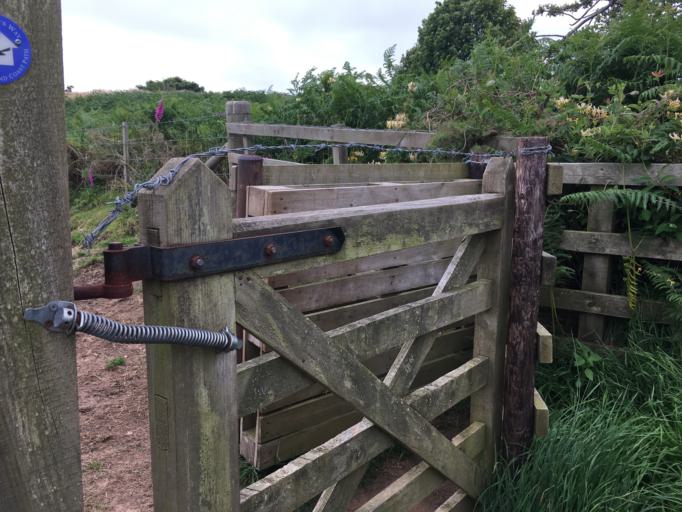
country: GB
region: England
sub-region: Northumberland
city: Belford
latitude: 55.6057
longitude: -1.8609
